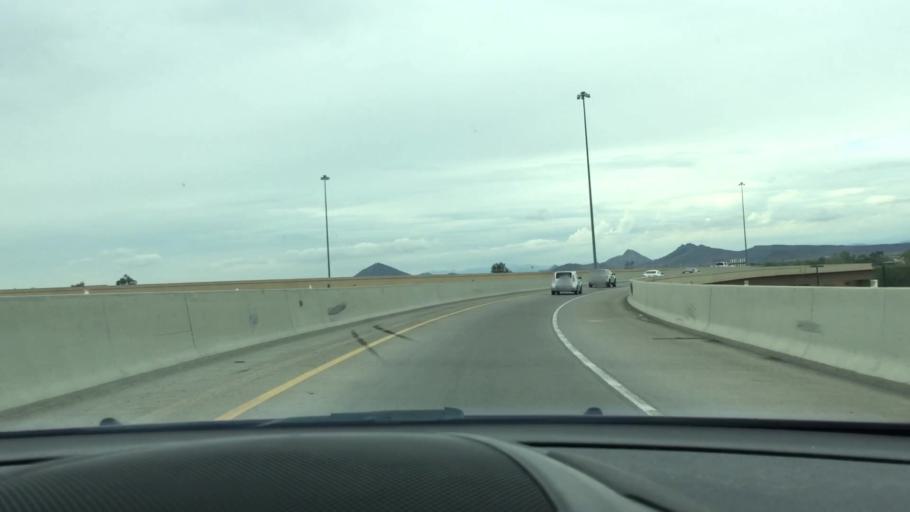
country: US
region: Arizona
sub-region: Maricopa County
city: Glendale
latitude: 33.6702
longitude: -112.1119
